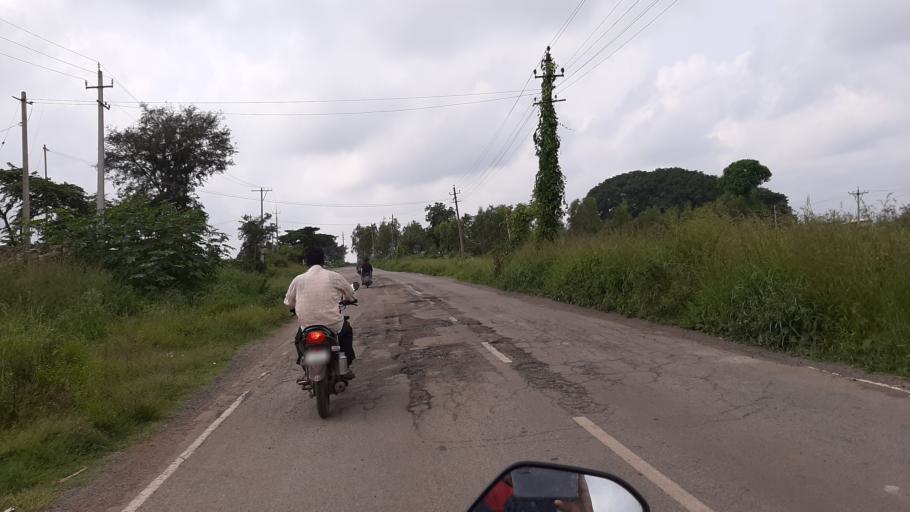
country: IN
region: Karnataka
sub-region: Ramanagara
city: Magadi
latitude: 12.9472
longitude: 77.2382
